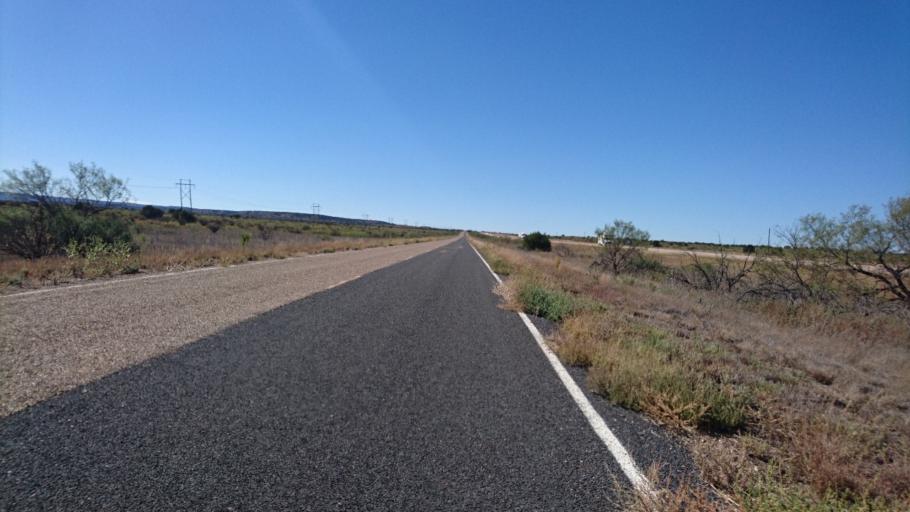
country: US
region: New Mexico
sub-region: Quay County
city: Tucumcari
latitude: 35.0757
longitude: -104.1398
